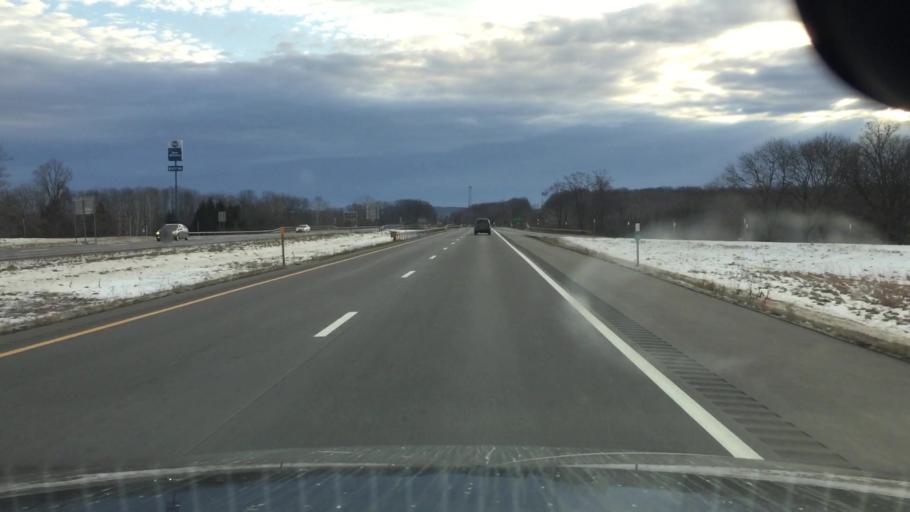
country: US
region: Pennsylvania
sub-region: Bradford County
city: South Waverly
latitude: 42.0000
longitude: -76.5272
